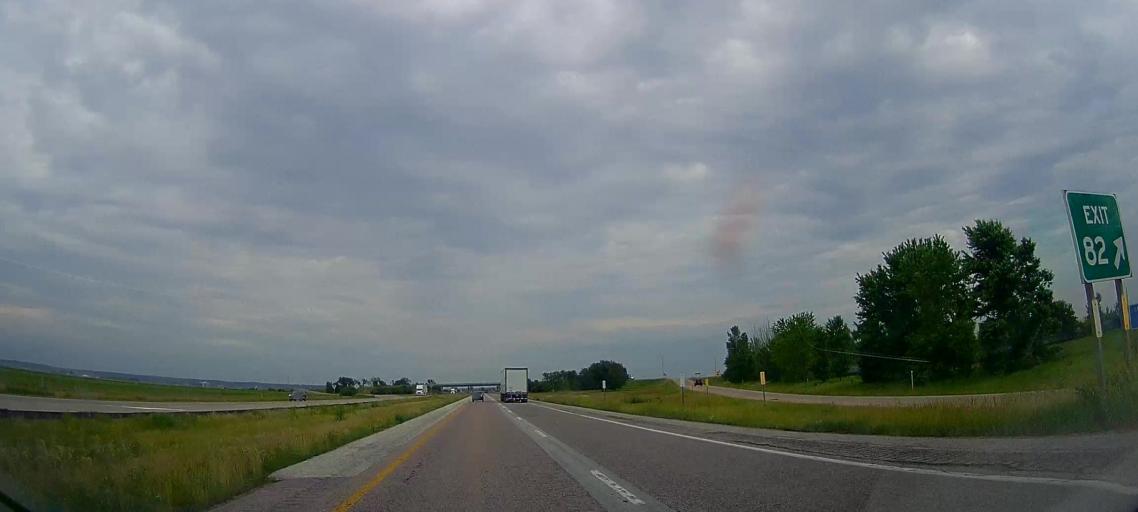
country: US
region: Iowa
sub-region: Harrison County
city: Missouri Valley
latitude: 41.6228
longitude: -95.9917
